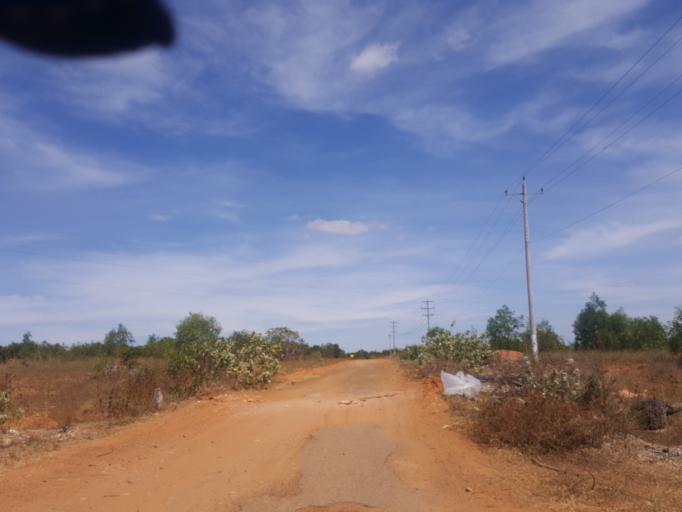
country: VN
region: Binh Thuan
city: Phan Thiet
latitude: 10.9610
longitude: 108.2153
